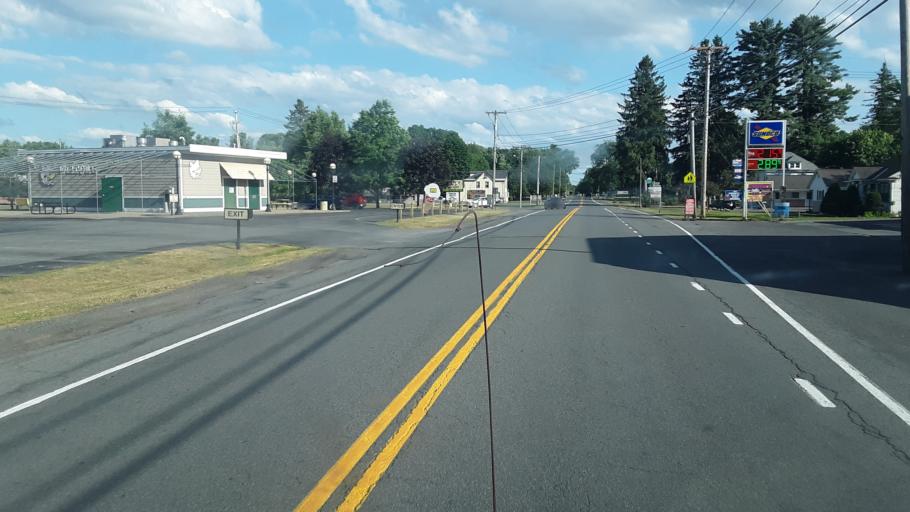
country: US
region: New York
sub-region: Oneida County
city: Rome
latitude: 43.2589
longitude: -75.4619
